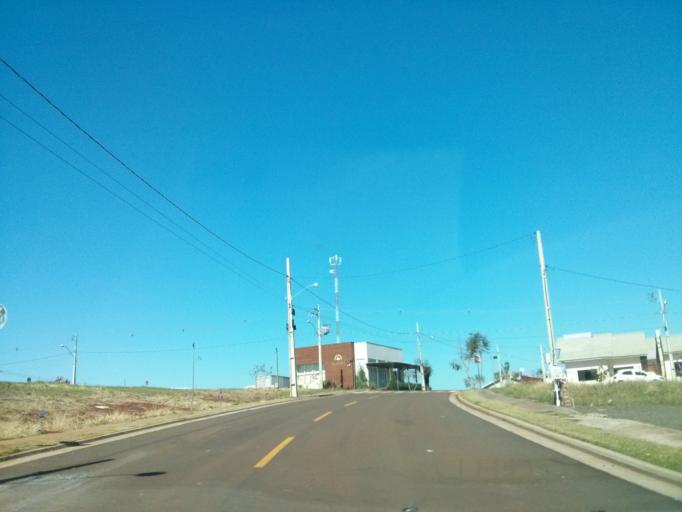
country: BR
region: Santa Catarina
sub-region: Chapeco
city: Chapeco
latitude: -27.0892
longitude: -52.7129
